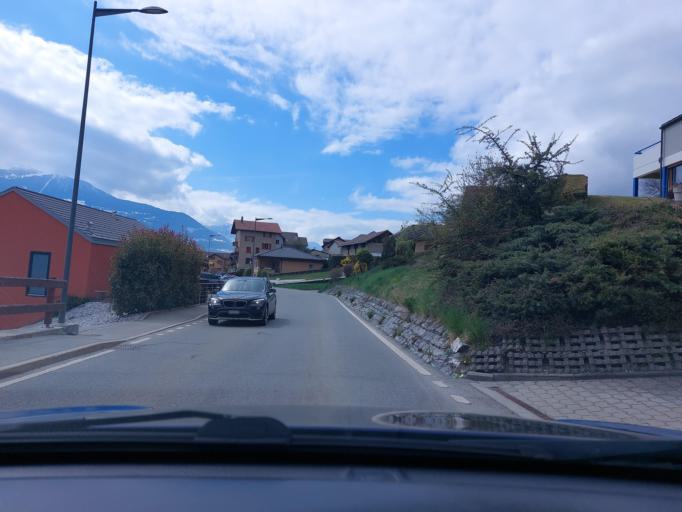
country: CH
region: Valais
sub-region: Conthey District
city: Conthey
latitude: 46.2439
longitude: 7.2968
